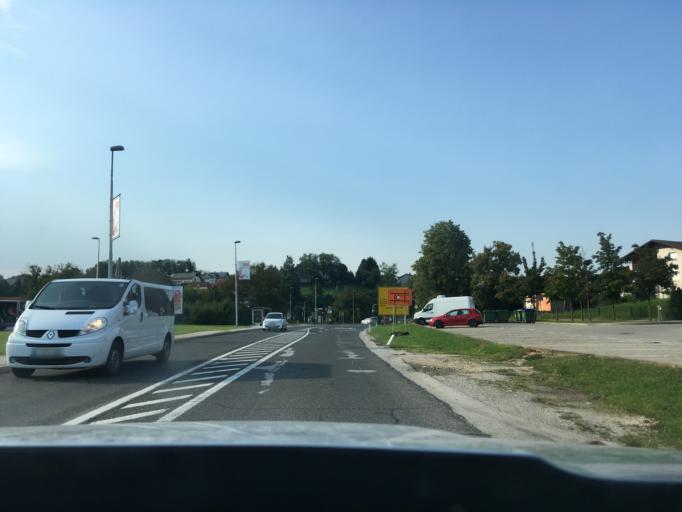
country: SI
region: Novo Mesto
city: Novo Mesto
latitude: 45.7984
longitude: 15.1803
